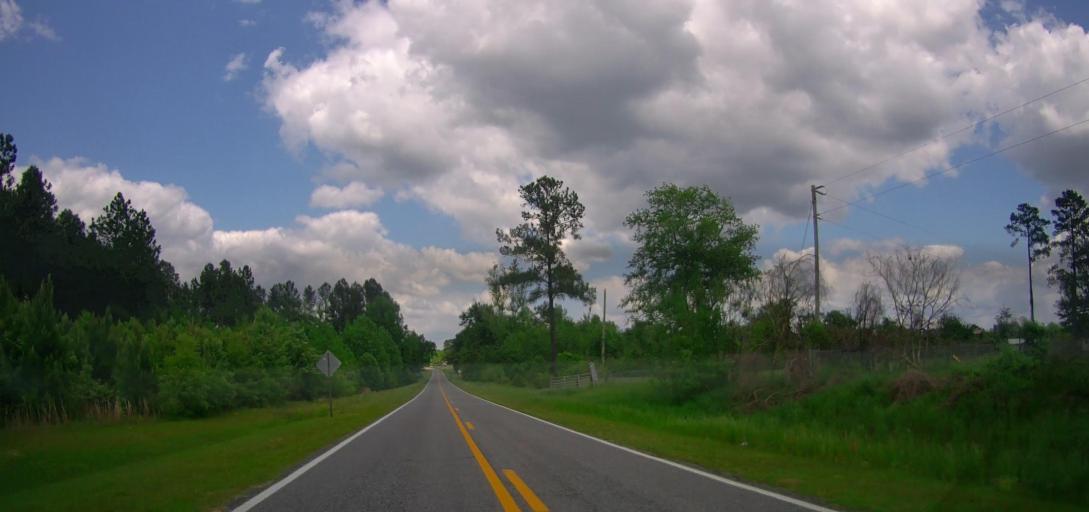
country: US
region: Georgia
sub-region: Laurens County
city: East Dublin
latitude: 32.5502
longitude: -82.8181
